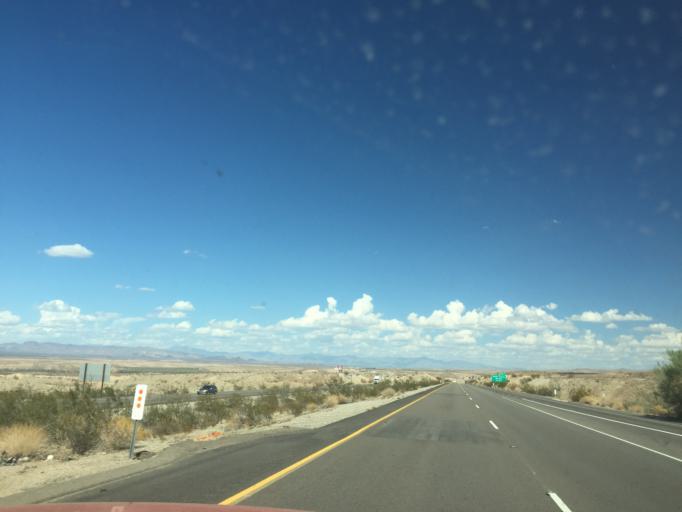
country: US
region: California
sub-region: San Bernardino County
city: Needles
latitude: 34.7175
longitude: -114.5079
